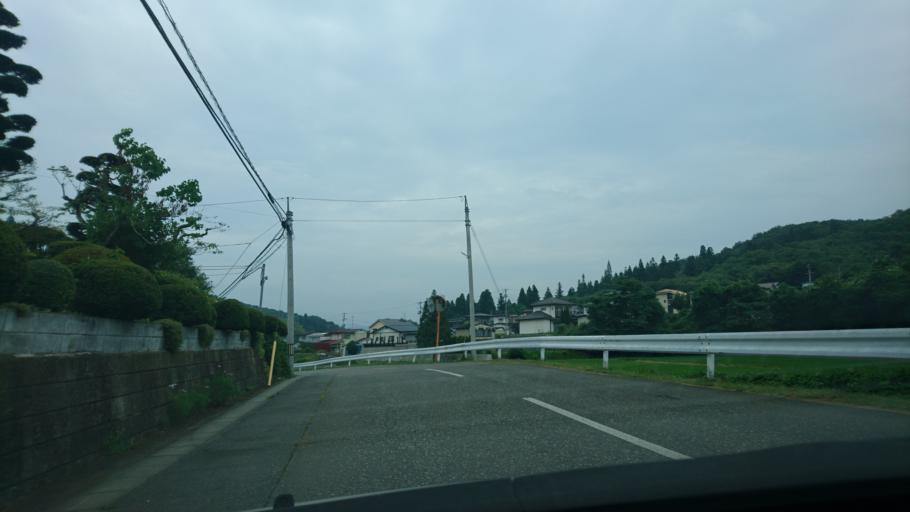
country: JP
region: Iwate
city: Ichinoseki
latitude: 38.9091
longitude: 141.1205
